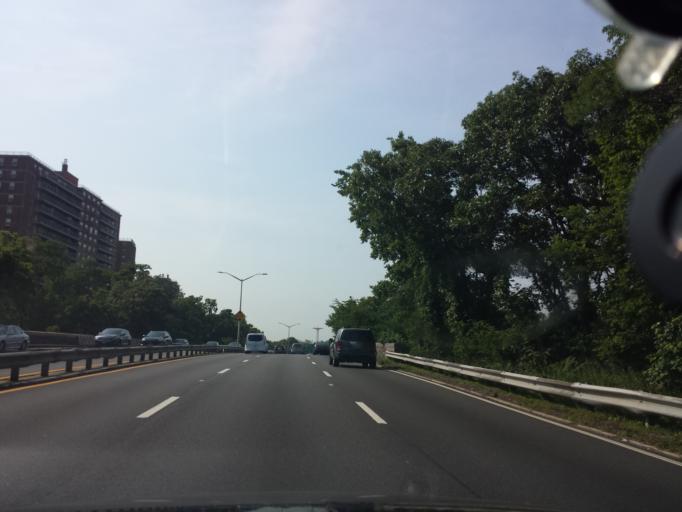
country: US
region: New York
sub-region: Kings County
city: Bensonhurst
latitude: 40.5901
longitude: -73.9932
